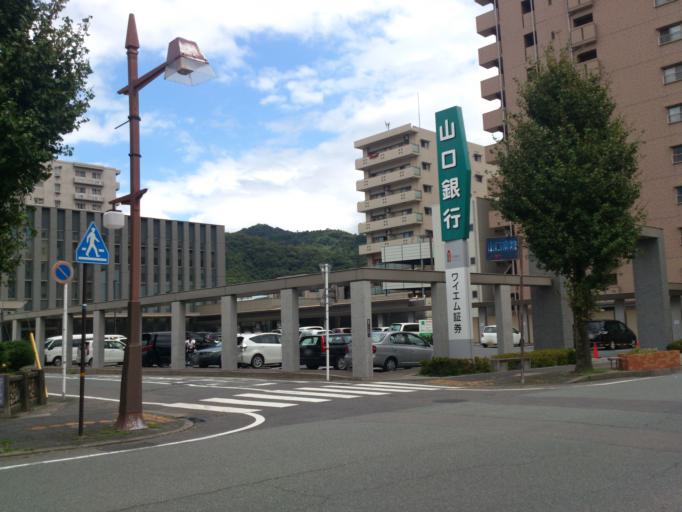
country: JP
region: Yamaguchi
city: Yamaguchi-shi
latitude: 34.1737
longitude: 131.4794
